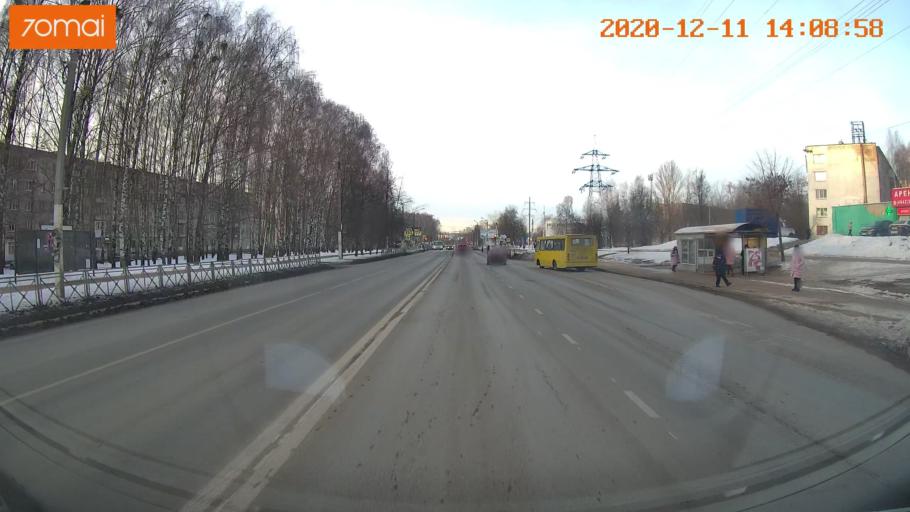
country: RU
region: Kostroma
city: Oktyabr'skiy
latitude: 57.7380
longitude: 40.9907
